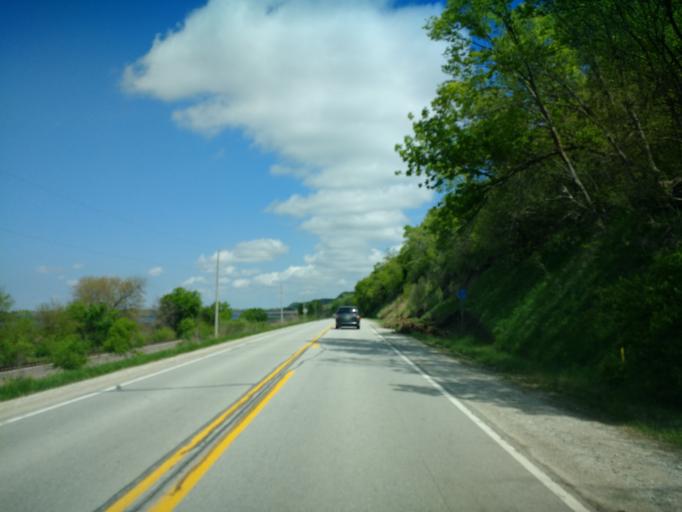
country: US
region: Iowa
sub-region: Harrison County
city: Missouri Valley
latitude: 41.4374
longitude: -95.8695
